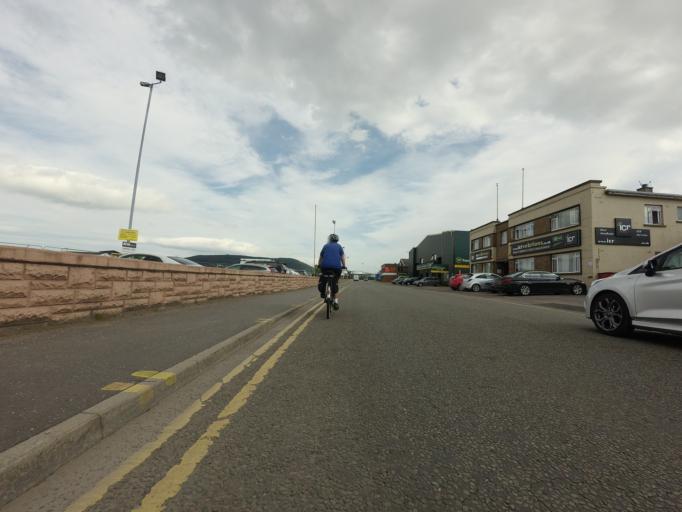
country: GB
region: Scotland
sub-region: Highland
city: Inverness
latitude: 57.4841
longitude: -4.2298
